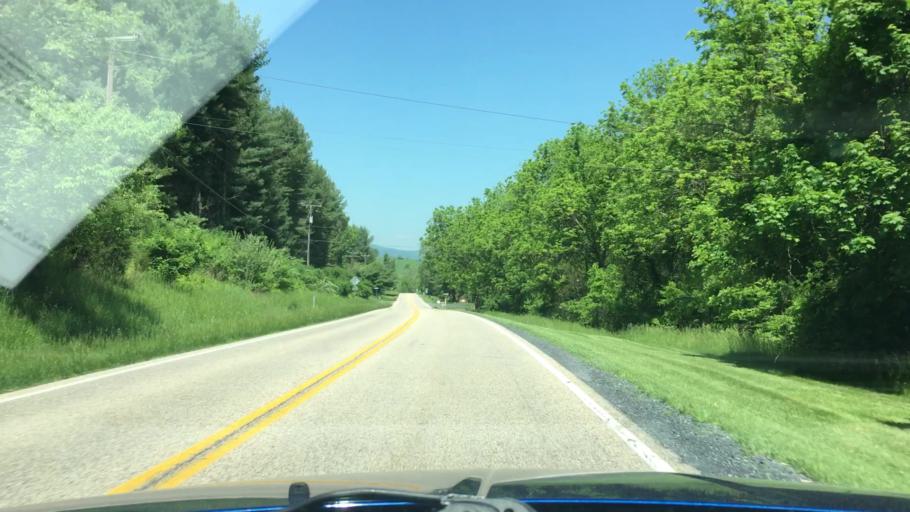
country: US
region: Virginia
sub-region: City of Staunton
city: Staunton
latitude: 38.1888
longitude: -79.1048
